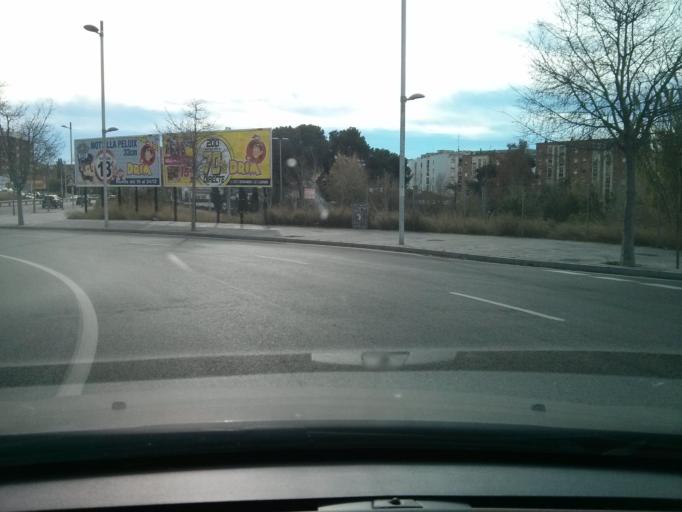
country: ES
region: Catalonia
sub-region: Provincia de Tarragona
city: Tarragona
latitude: 41.1247
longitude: 1.2425
